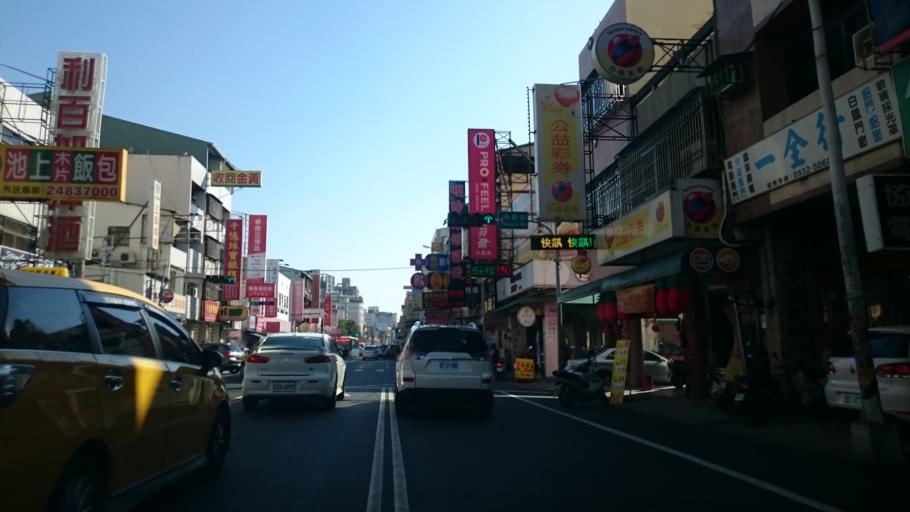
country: TW
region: Taiwan
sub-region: Taichung City
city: Taichung
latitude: 24.1145
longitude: 120.6898
